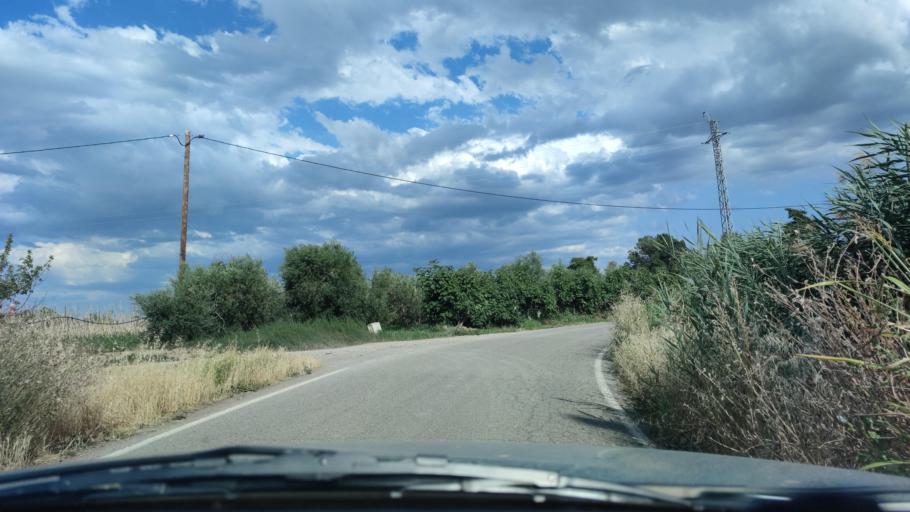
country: ES
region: Catalonia
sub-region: Provincia de Lleida
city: Alpicat
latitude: 41.6283
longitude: 0.5727
